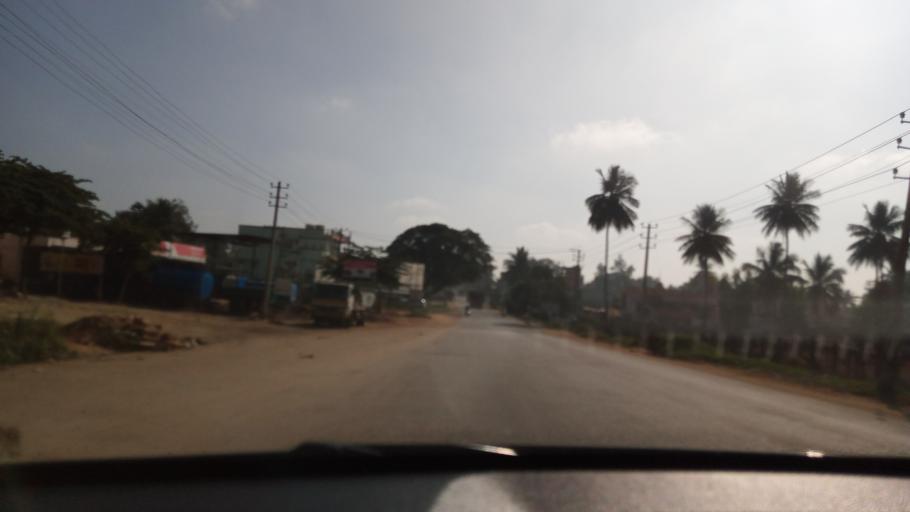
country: IN
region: Karnataka
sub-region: Bangalore Rural
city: Devanhalli
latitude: 13.2574
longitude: 77.7137
